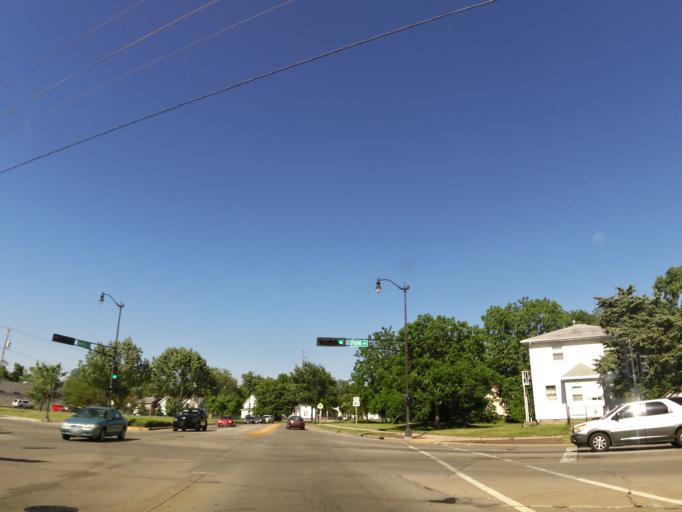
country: US
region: Wisconsin
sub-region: Rock County
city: Beloit
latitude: 42.5105
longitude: -89.0271
